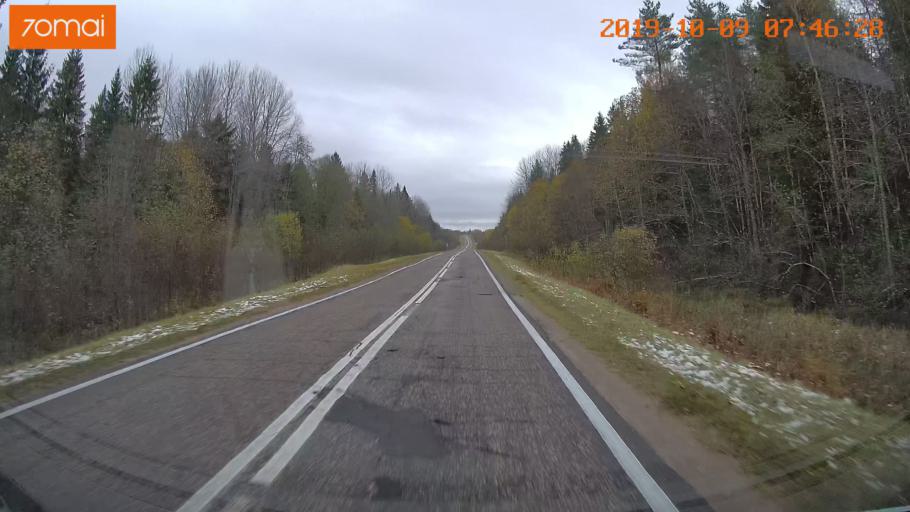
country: RU
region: Jaroslavl
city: Kukoboy
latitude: 58.6562
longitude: 39.7882
